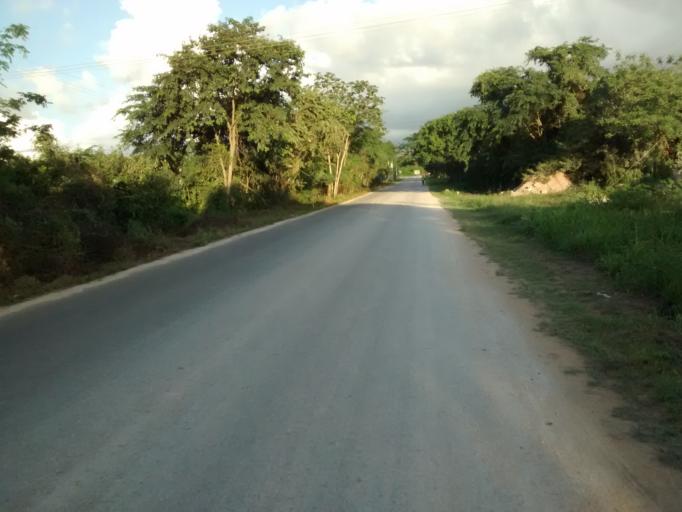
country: MX
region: Yucatan
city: Valladolid
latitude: 20.7311
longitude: -88.2062
